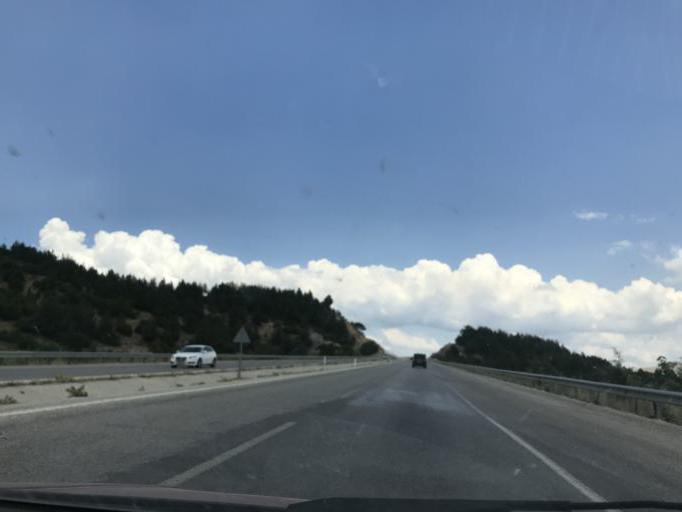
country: TR
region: Denizli
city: Tavas
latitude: 37.6141
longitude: 29.1599
